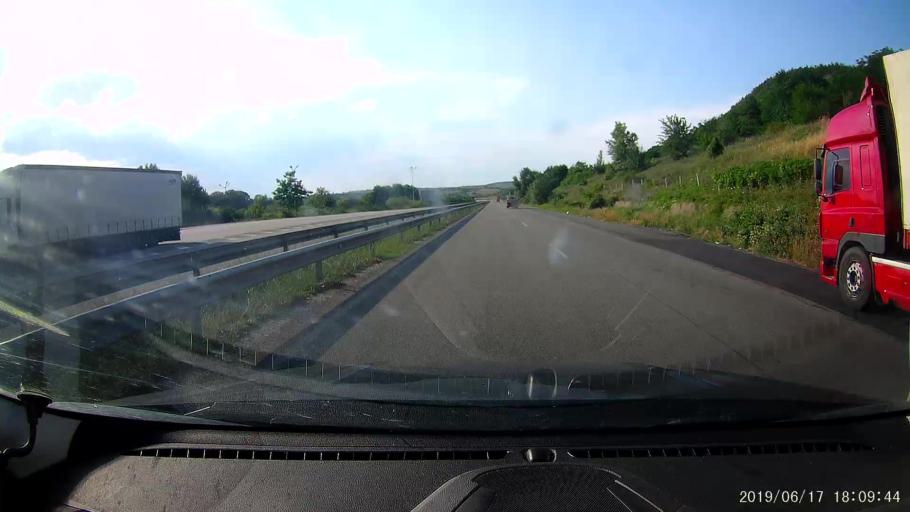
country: BG
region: Khaskovo
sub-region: Obshtina Lyubimets
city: Lyubimets
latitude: 41.8641
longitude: 26.0867
